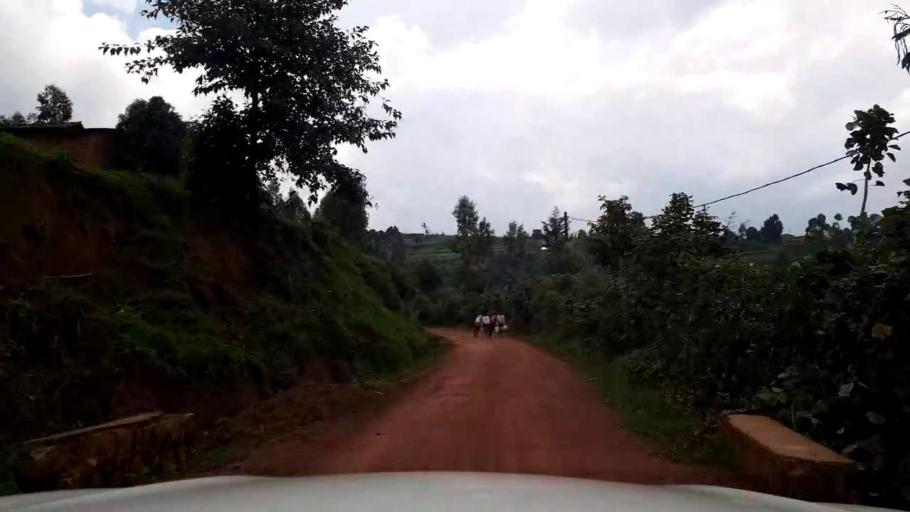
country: RW
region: Northern Province
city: Byumba
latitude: -1.4856
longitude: 29.9061
